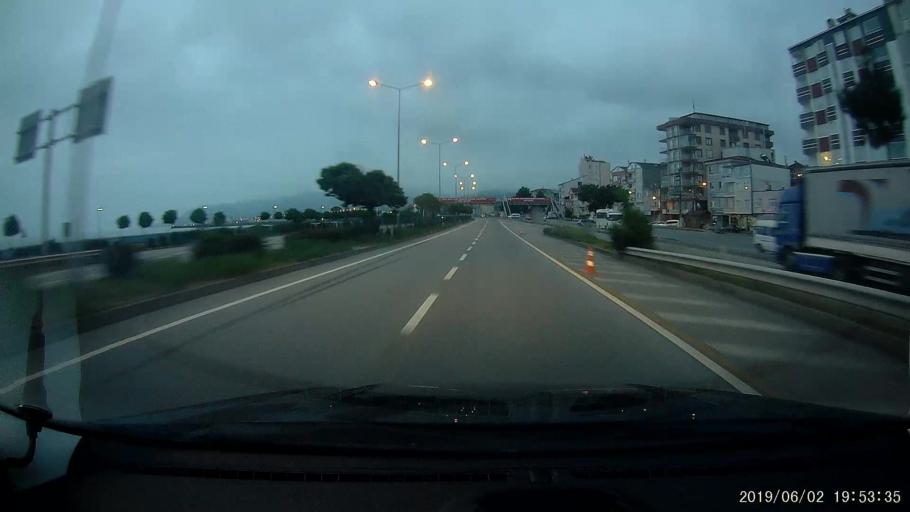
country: TR
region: Trabzon
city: Espiye
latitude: 40.9501
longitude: 38.7097
